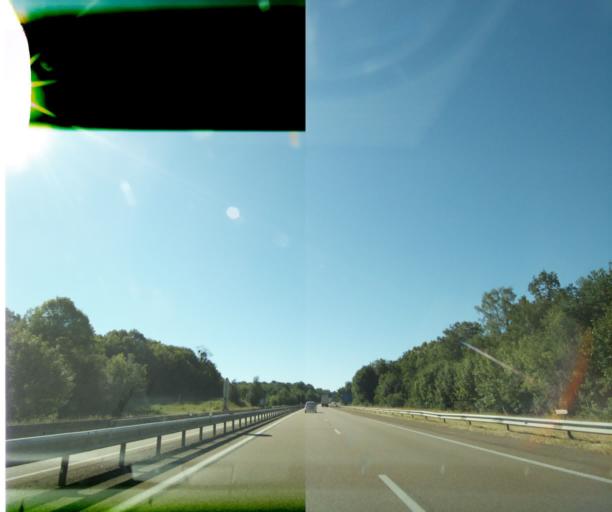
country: FR
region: Champagne-Ardenne
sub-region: Departement de la Haute-Marne
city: Chamarandes-Choignes
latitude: 48.0267
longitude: 5.0891
